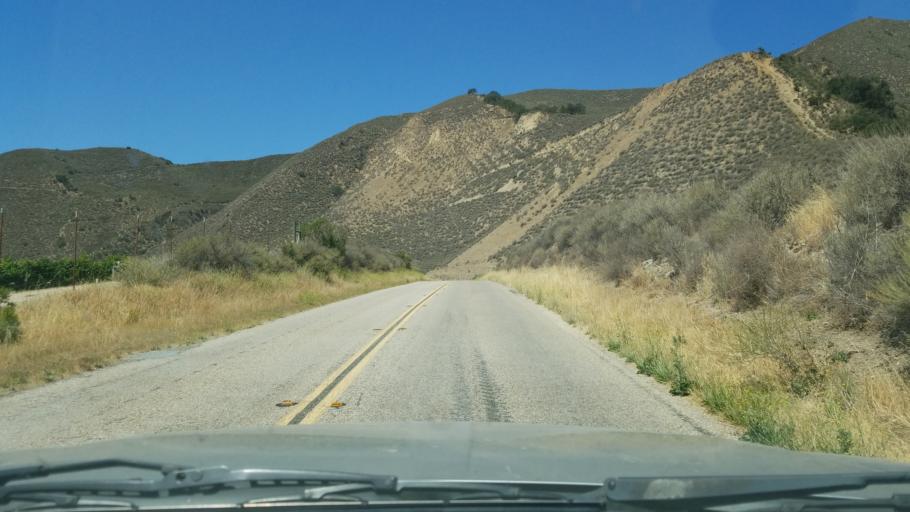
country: US
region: California
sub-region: Monterey County
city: Greenfield
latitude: 36.2788
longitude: -121.3292
